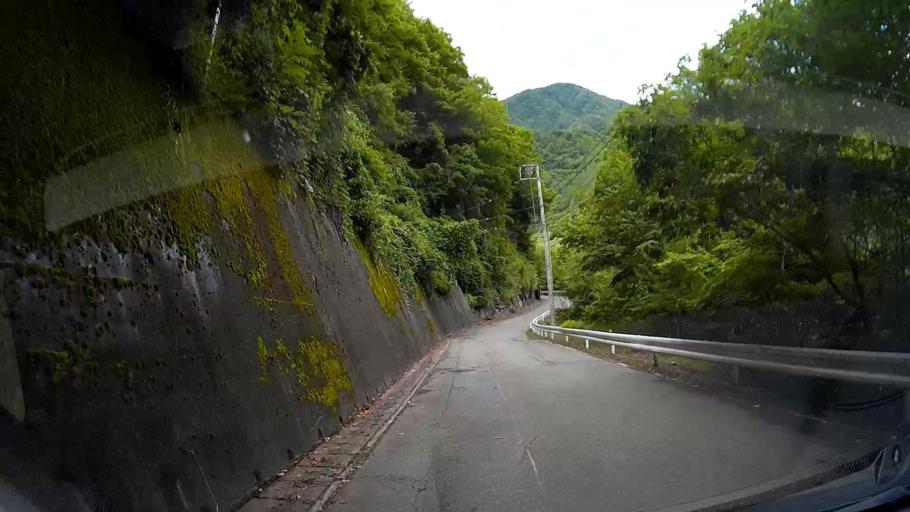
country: JP
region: Shizuoka
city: Shizuoka-shi
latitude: 35.3079
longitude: 138.1922
